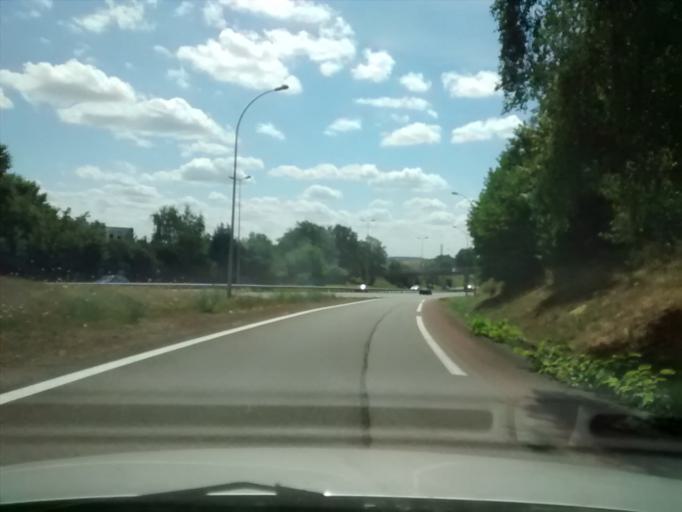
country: FR
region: Pays de la Loire
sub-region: Departement de la Sarthe
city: La Chapelle-Saint-Aubin
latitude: 48.0116
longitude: 0.1705
